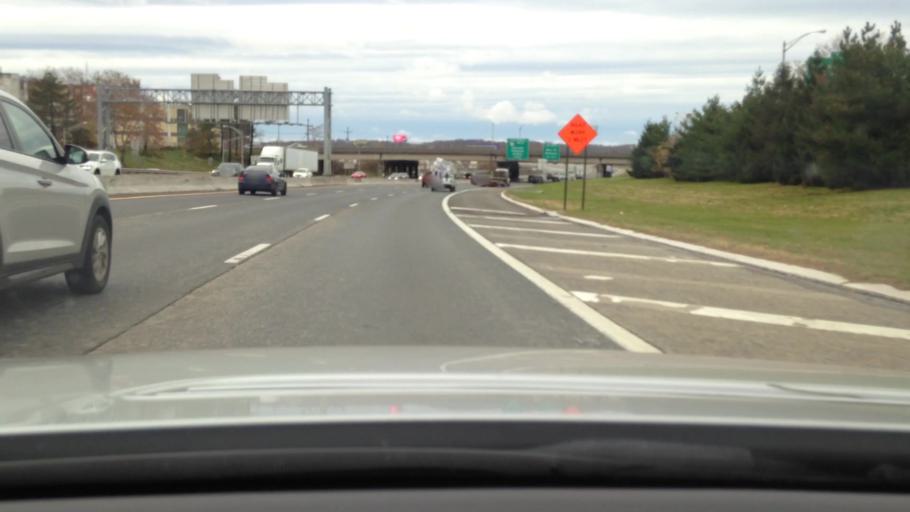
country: US
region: New Jersey
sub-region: Passaic County
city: Paterson
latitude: 40.9024
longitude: -74.1562
